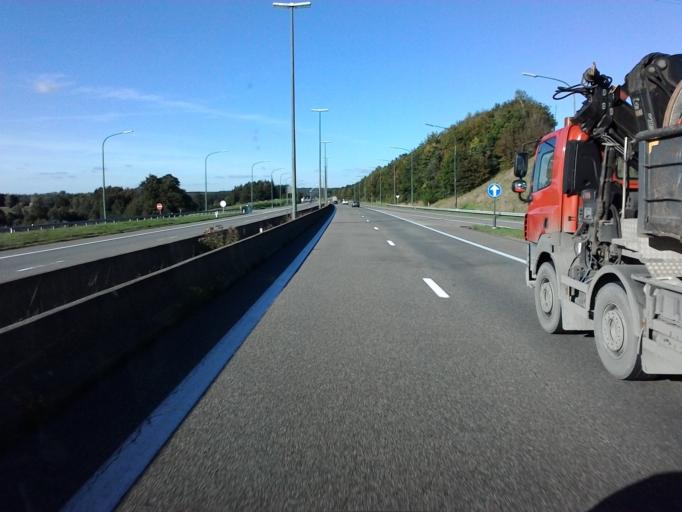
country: BE
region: Wallonia
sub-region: Province du Luxembourg
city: Bastogne
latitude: 50.0209
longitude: 5.6971
